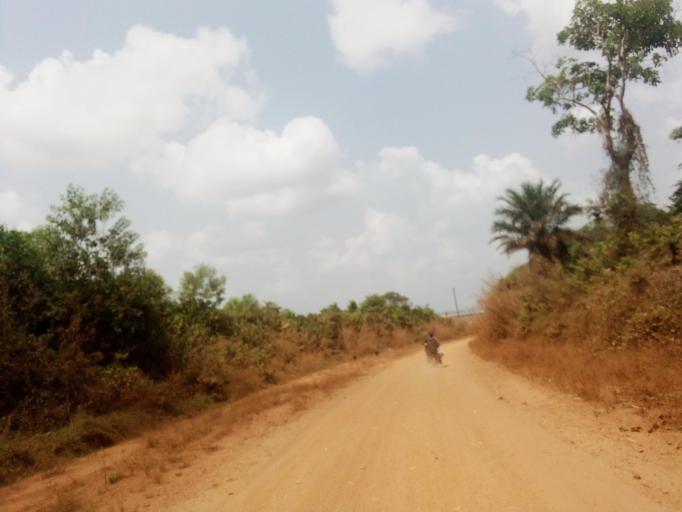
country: SL
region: Southern Province
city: Mogbwemo
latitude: 7.6649
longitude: -12.2782
